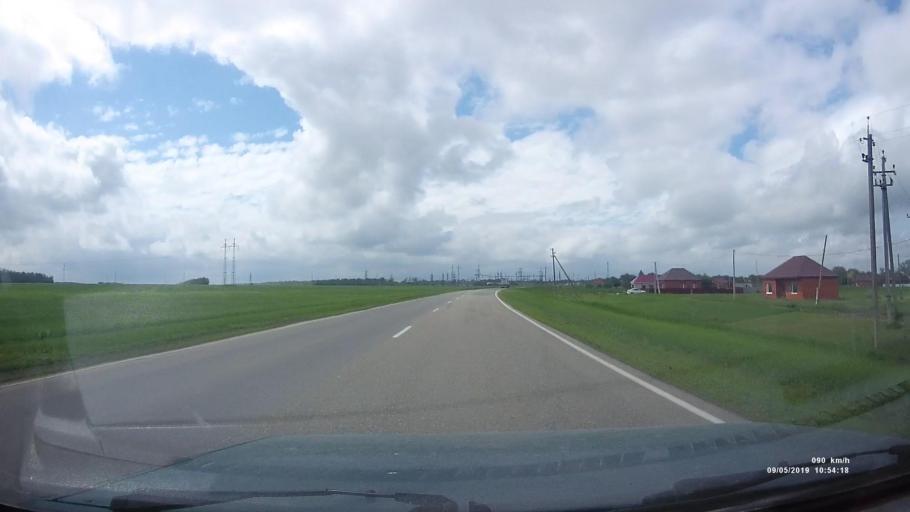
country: RU
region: Rostov
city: Peshkovo
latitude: 46.8791
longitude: 39.3322
